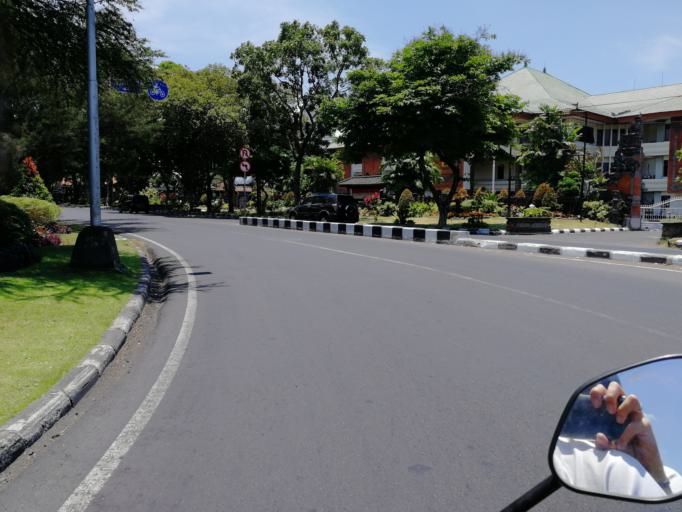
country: ID
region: Bali
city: Denpasar
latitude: -8.6696
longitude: 115.2216
